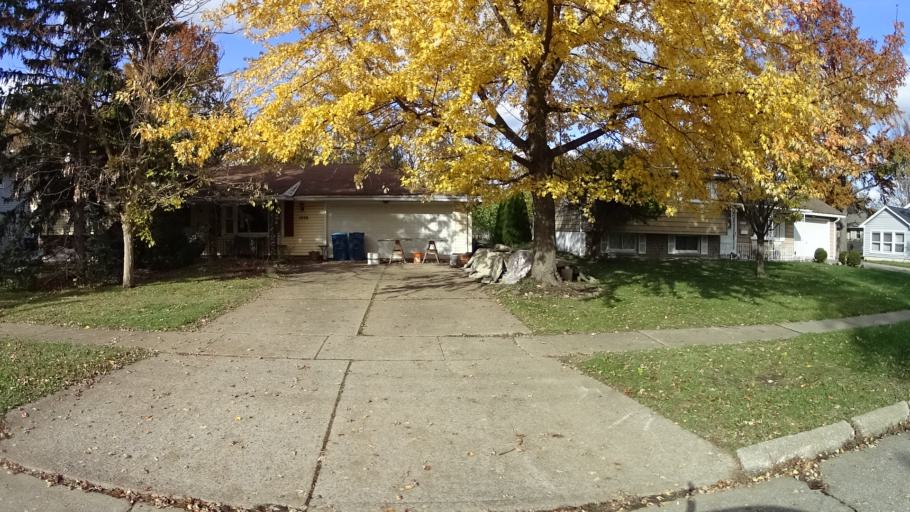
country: US
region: Ohio
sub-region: Lorain County
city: Lorain
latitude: 41.4313
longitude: -82.1905
